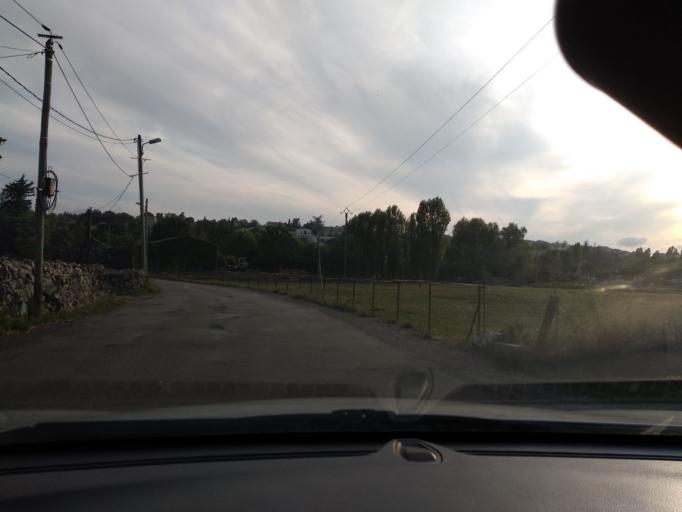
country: FR
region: Provence-Alpes-Cote d'Azur
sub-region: Departement des Alpes-Maritimes
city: Saint-Cezaire-sur-Siagne
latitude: 43.6527
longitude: 6.7996
